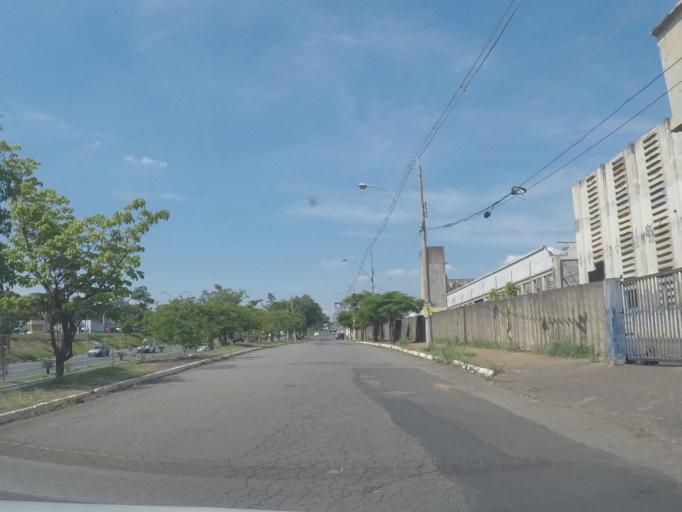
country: BR
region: Sao Paulo
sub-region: Sumare
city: Sumare
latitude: -22.8179
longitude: -47.2613
